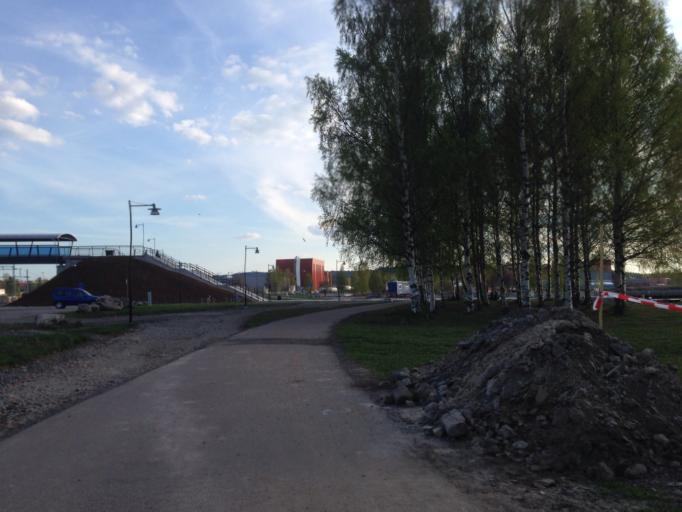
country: SE
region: Dalarna
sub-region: Ludvika Kommun
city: Ludvika
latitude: 60.1514
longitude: 15.1823
